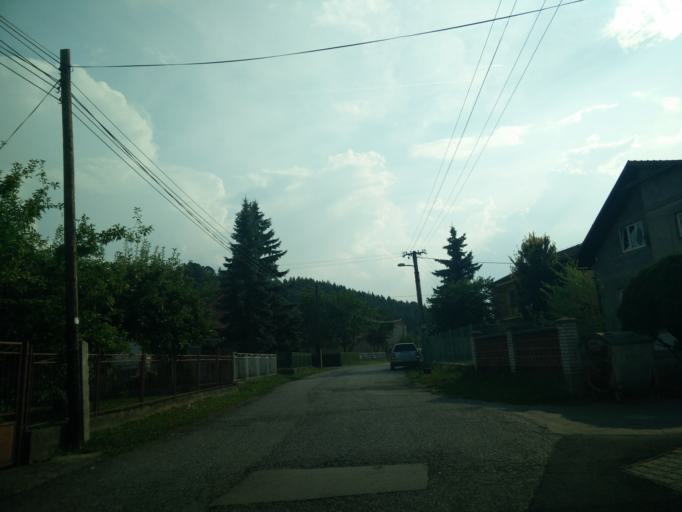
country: SK
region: Banskobystricky
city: Ziar nad Hronom
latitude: 48.5394
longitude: 18.7843
